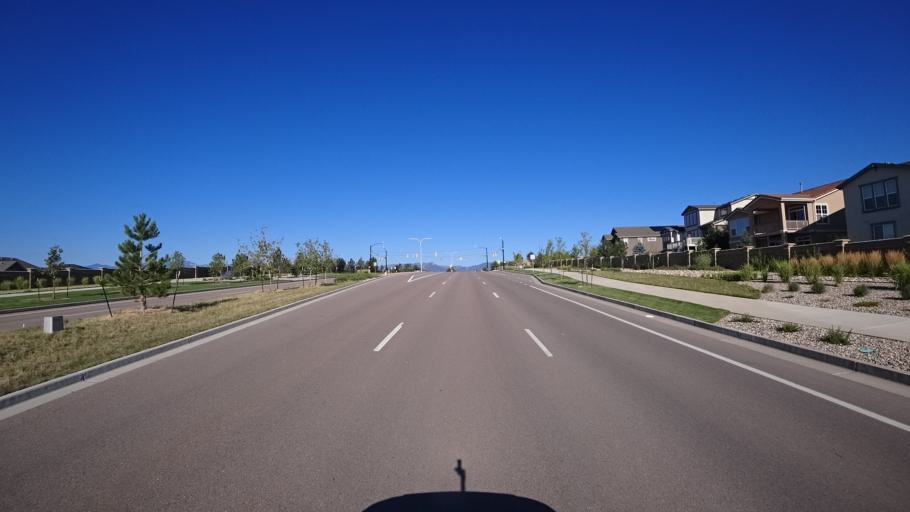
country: US
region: Colorado
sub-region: El Paso County
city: Black Forest
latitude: 38.9712
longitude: -104.7307
